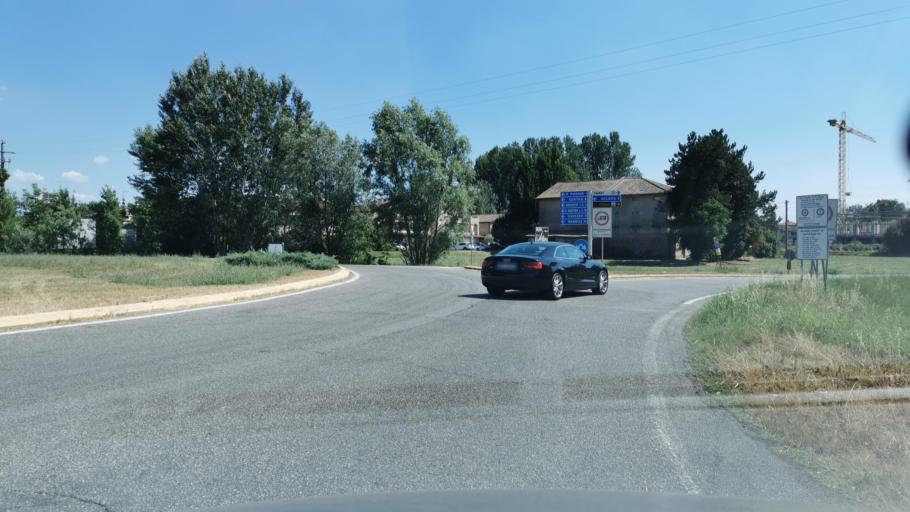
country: IT
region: Emilia-Romagna
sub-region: Provincia di Modena
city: Sam Marino
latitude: 44.8012
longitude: 10.9037
